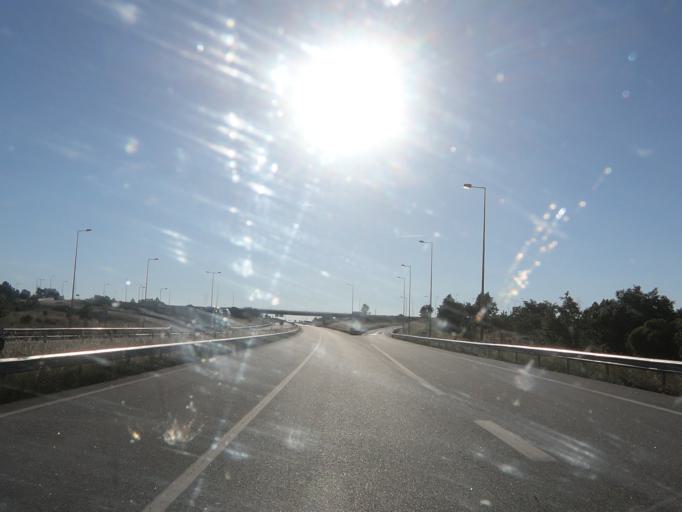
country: ES
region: Castille and Leon
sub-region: Provincia de Salamanca
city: Fuentes de Onoro
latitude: 40.6069
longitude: -6.9788
